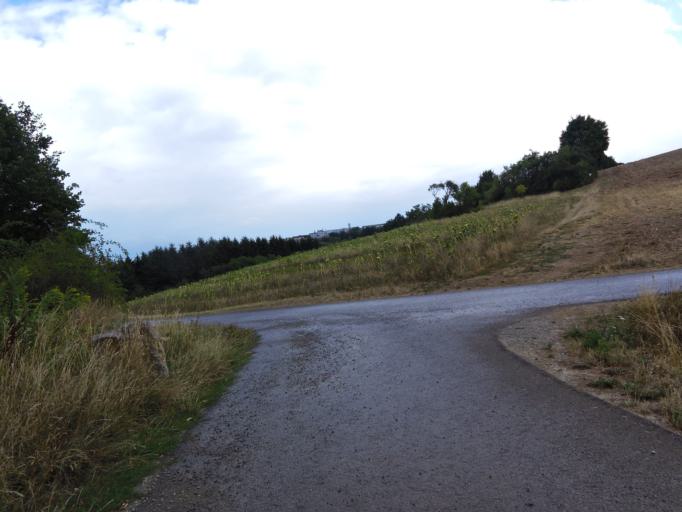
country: DE
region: Bavaria
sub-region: Regierungsbezirk Unterfranken
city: Waldbuttelbrunn
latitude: 49.7764
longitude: 9.8608
